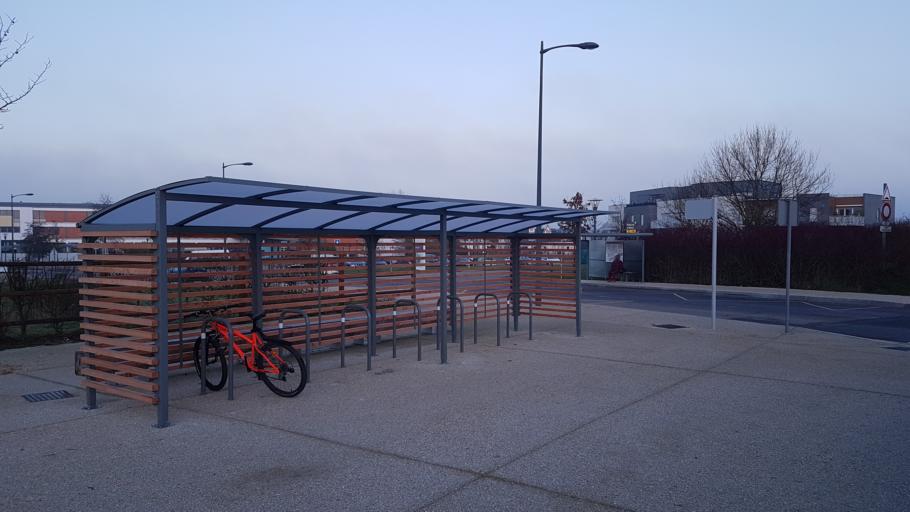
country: FR
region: Haute-Normandie
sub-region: Departement de la Seine-Maritime
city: Isneauville
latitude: 49.4917
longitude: 1.1440
